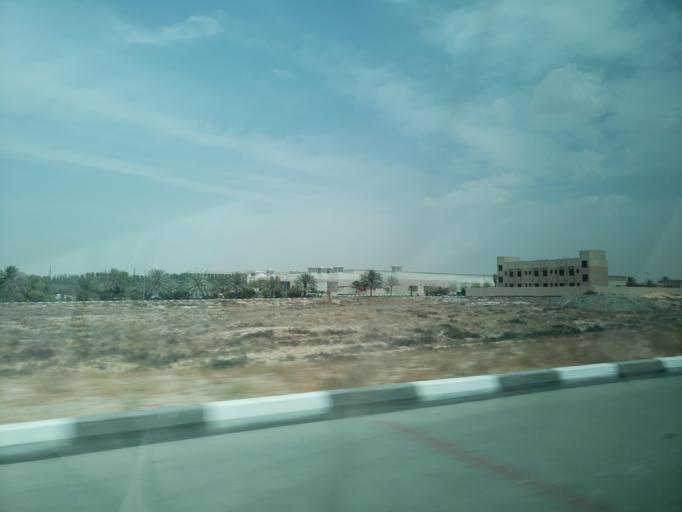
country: AE
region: Ash Shariqah
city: Sharjah
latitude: 25.3156
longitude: 55.5115
